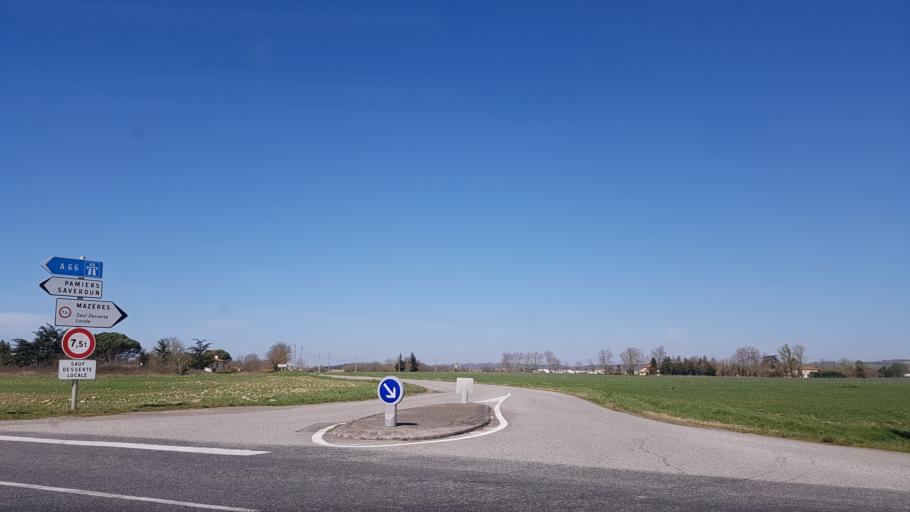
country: FR
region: Midi-Pyrenees
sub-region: Departement de l'Ariege
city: Mazeres
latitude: 43.2292
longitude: 1.6874
